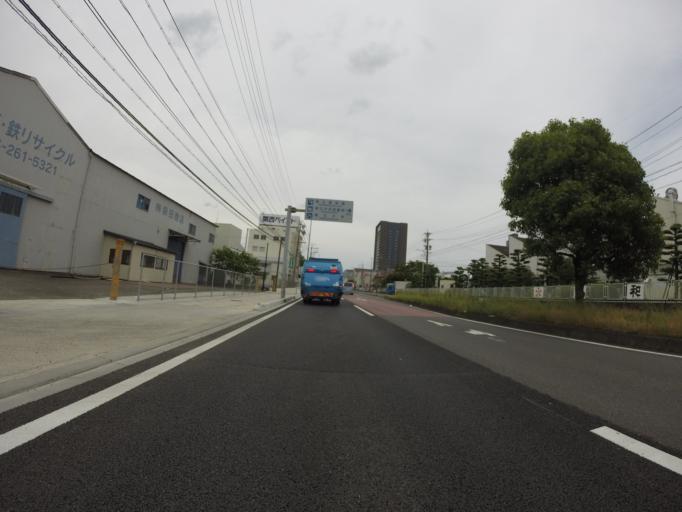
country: JP
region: Shizuoka
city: Shizuoka-shi
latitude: 35.0021
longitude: 138.4358
